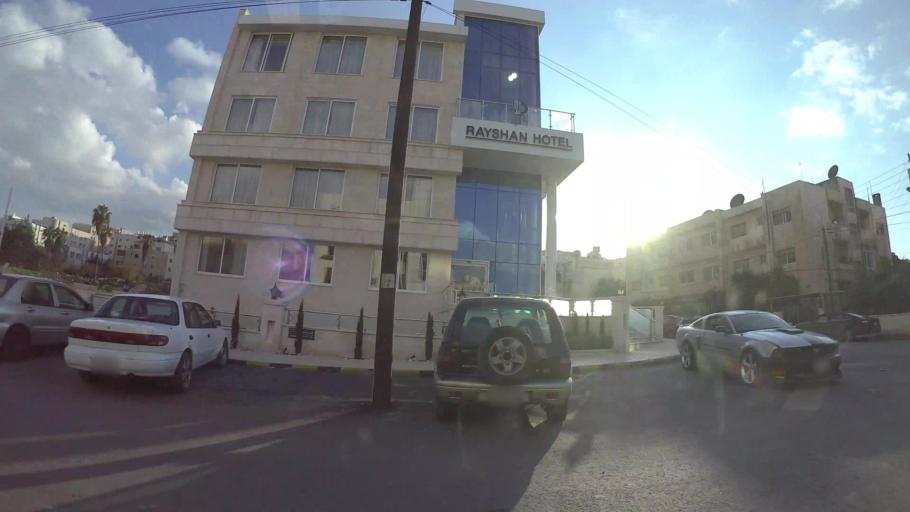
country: JO
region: Amman
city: Al Jubayhah
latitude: 31.9823
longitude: 35.8906
